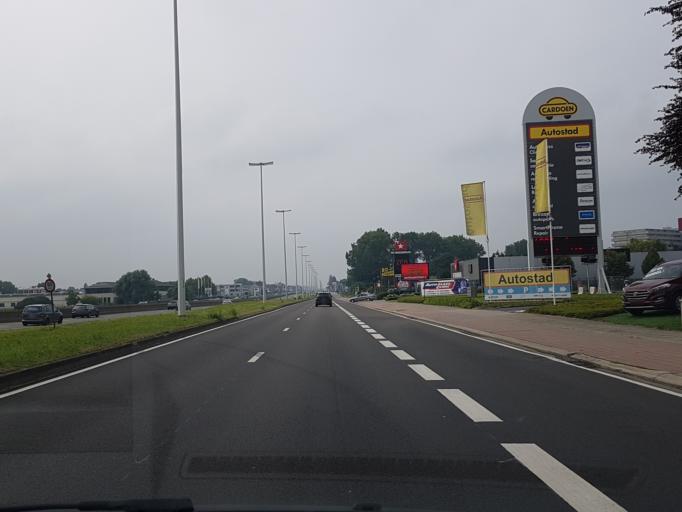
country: BE
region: Flanders
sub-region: Provincie Antwerpen
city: Aartselaar
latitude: 51.1505
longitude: 4.3812
